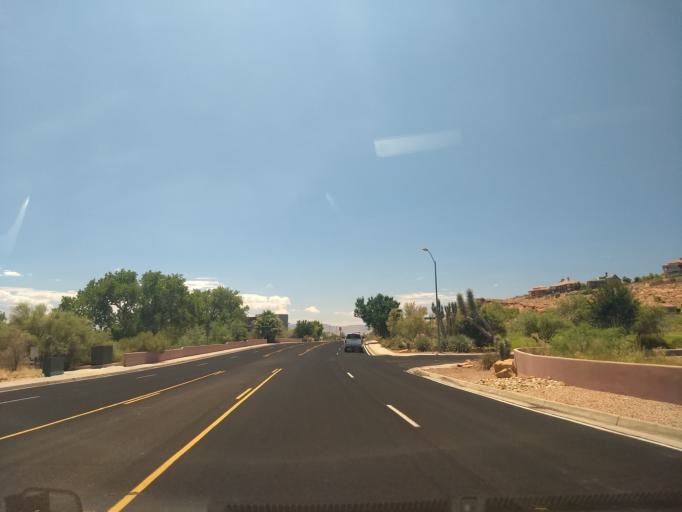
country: US
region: Utah
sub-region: Washington County
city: Washington
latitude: 37.1355
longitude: -113.5263
